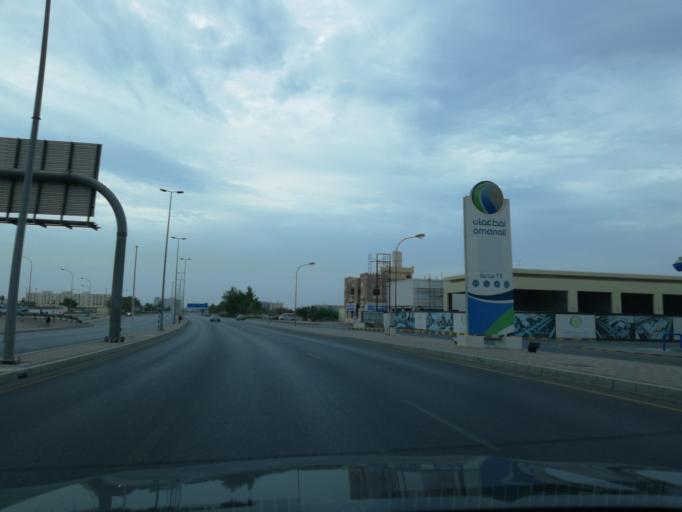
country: OM
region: Muhafazat Masqat
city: Bawshar
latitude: 23.5762
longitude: 58.3828
